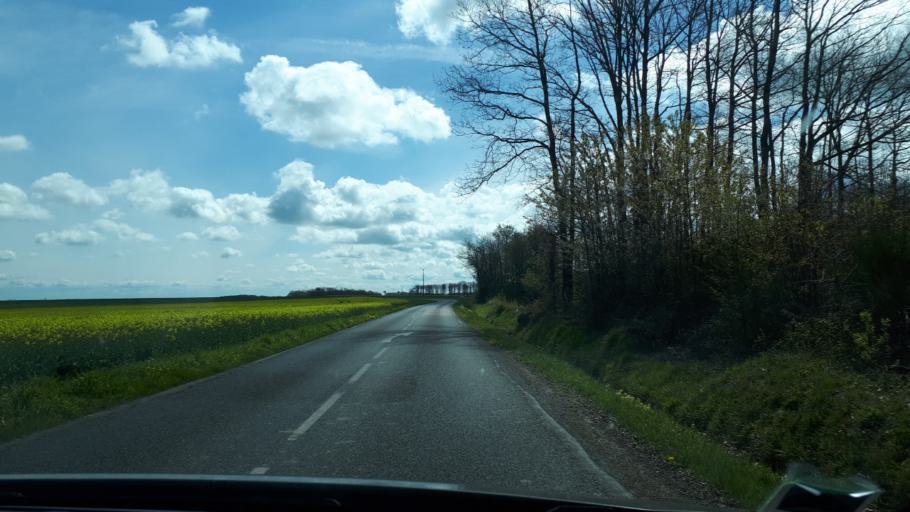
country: FR
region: Centre
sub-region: Departement du Loir-et-Cher
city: Lunay
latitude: 47.8327
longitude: 0.9101
